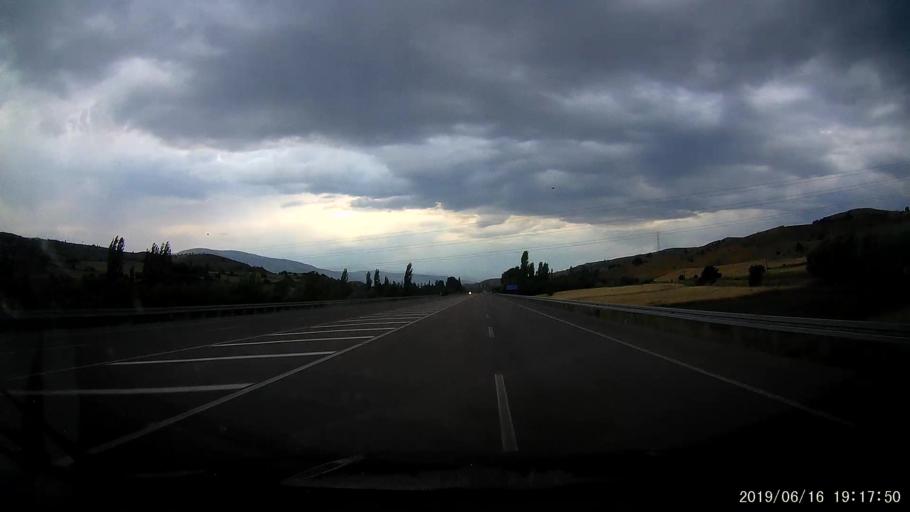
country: TR
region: Sivas
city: Akincilar
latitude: 40.0938
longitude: 38.4748
